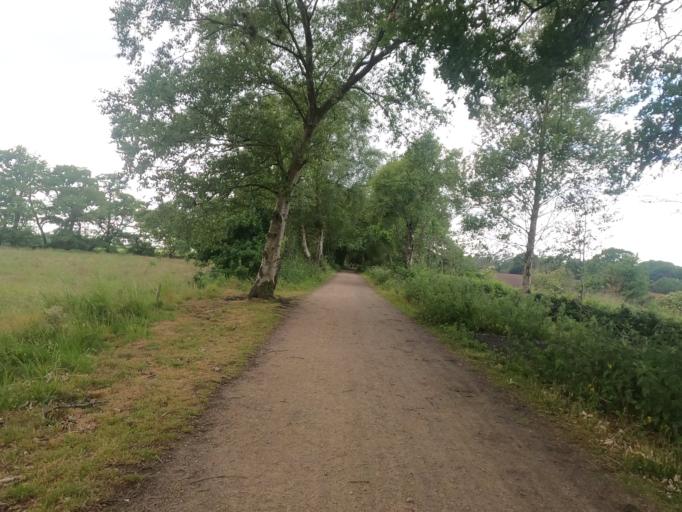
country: GB
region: England
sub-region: Cheshire West and Chester
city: Over
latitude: 53.2045
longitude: -2.5656
